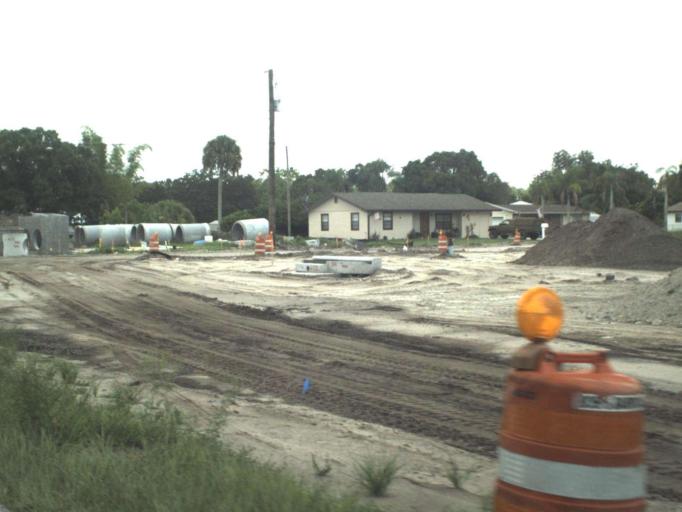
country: US
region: Florida
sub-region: Saint Lucie County
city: White City
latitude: 27.3742
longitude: -80.3589
